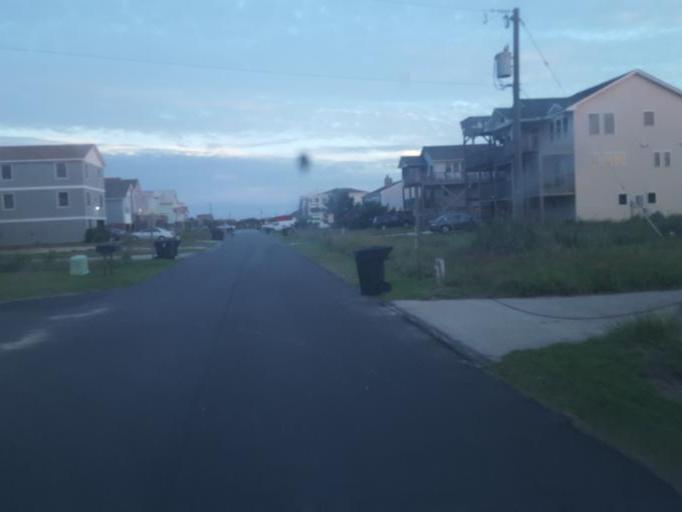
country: US
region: North Carolina
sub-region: Dare County
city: Kitty Hawk
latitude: 36.0724
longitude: -75.6955
